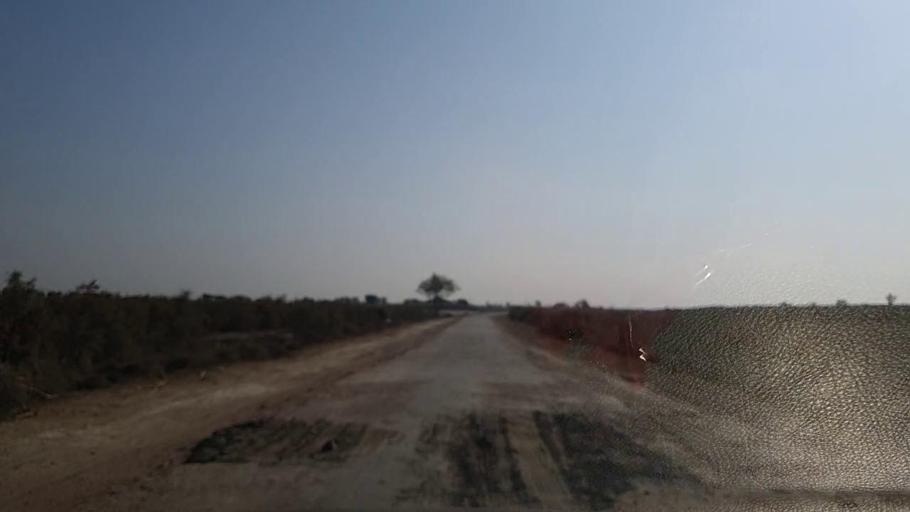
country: PK
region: Sindh
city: Sanghar
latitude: 25.9929
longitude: 69.0240
